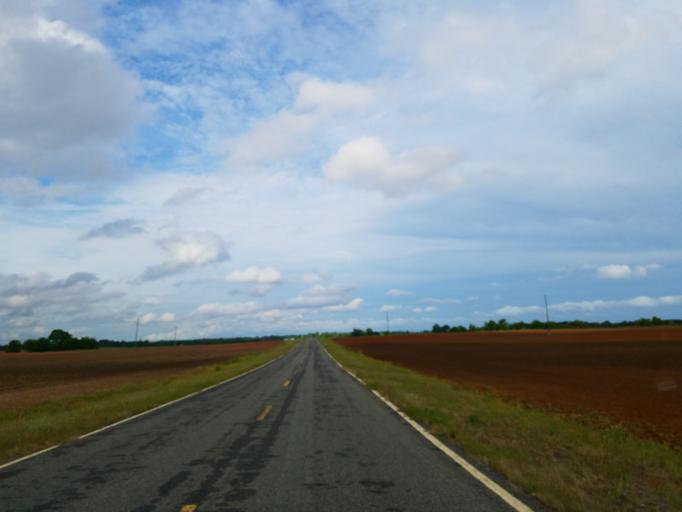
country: US
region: Georgia
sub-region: Dooly County
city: Unadilla
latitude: 32.2128
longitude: -83.7582
